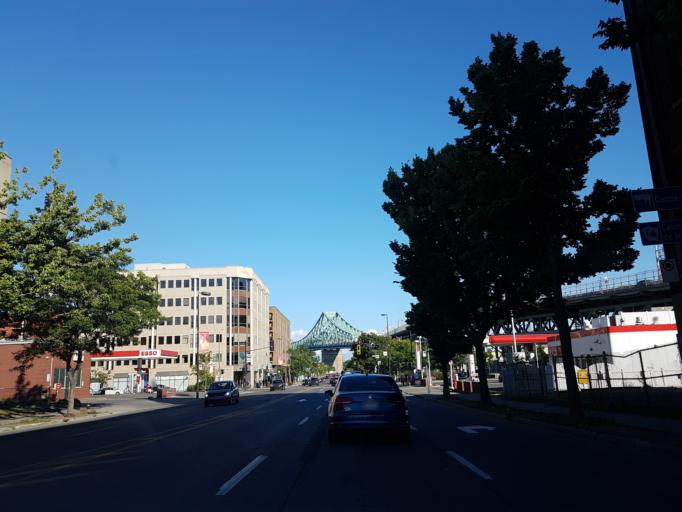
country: CA
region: Quebec
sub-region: Monteregie
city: Longueuil
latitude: 45.5259
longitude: -73.5528
